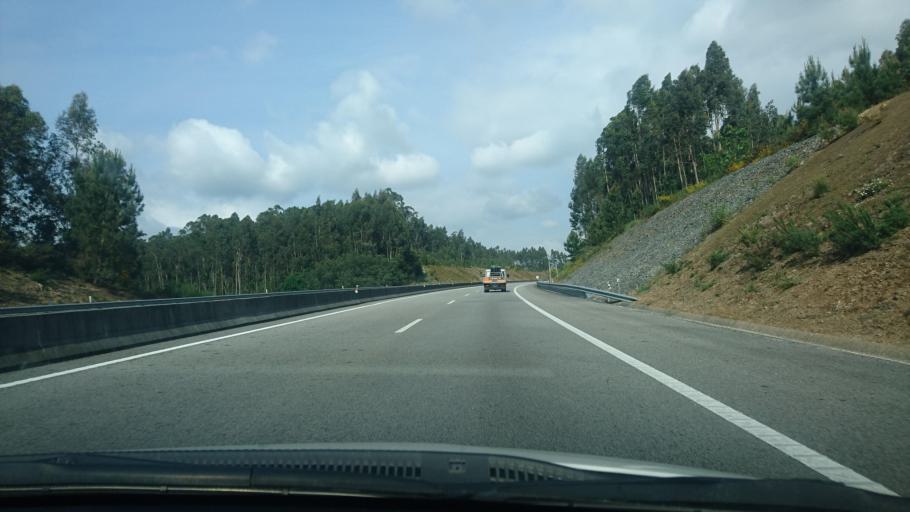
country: PT
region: Aveiro
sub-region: Santa Maria da Feira
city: Argoncilhe
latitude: 41.0202
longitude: -8.5253
